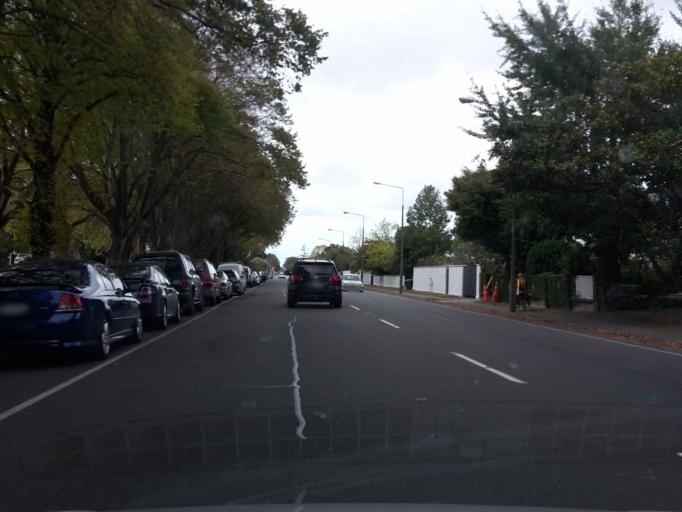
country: NZ
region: Canterbury
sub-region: Christchurch City
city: Christchurch
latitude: -43.5128
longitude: 172.6117
